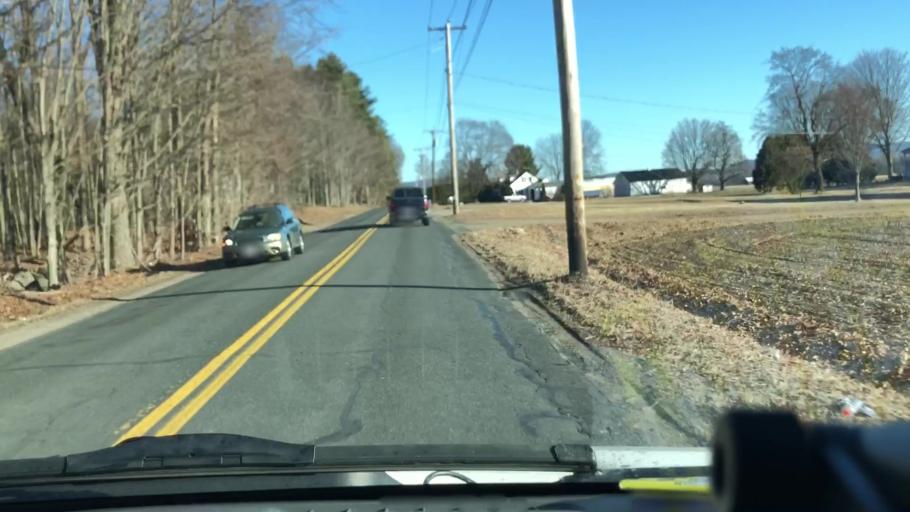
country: US
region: Massachusetts
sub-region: Hampshire County
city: North Amherst
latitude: 42.3936
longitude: -72.5472
